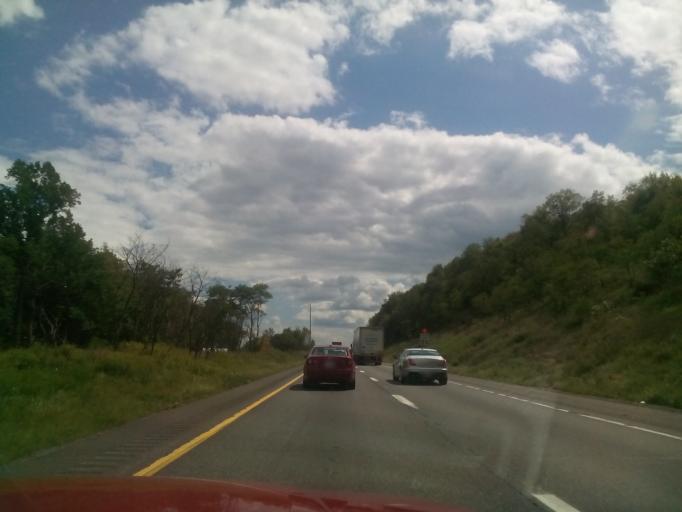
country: US
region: Pennsylvania
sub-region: Monroe County
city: Tannersville
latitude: 41.0467
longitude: -75.3150
